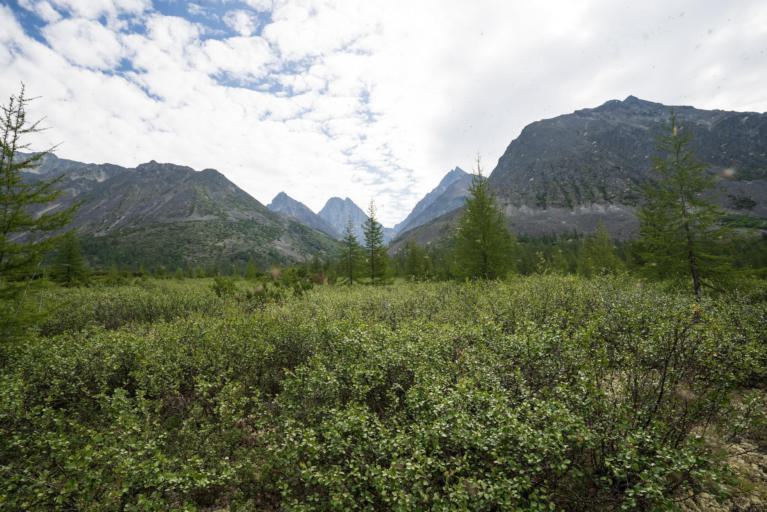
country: RU
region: Transbaikal Territory
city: Chara
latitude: 56.8667
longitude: 117.3023
